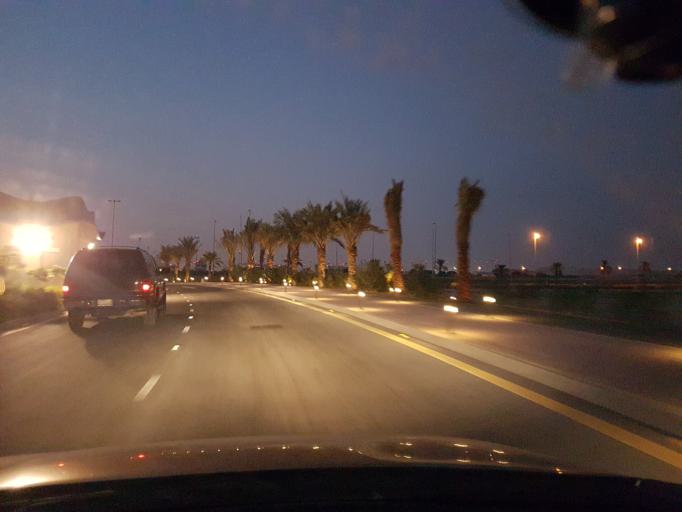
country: BH
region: Central Governorate
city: Dar Kulayb
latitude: 26.0192
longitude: 50.5097
